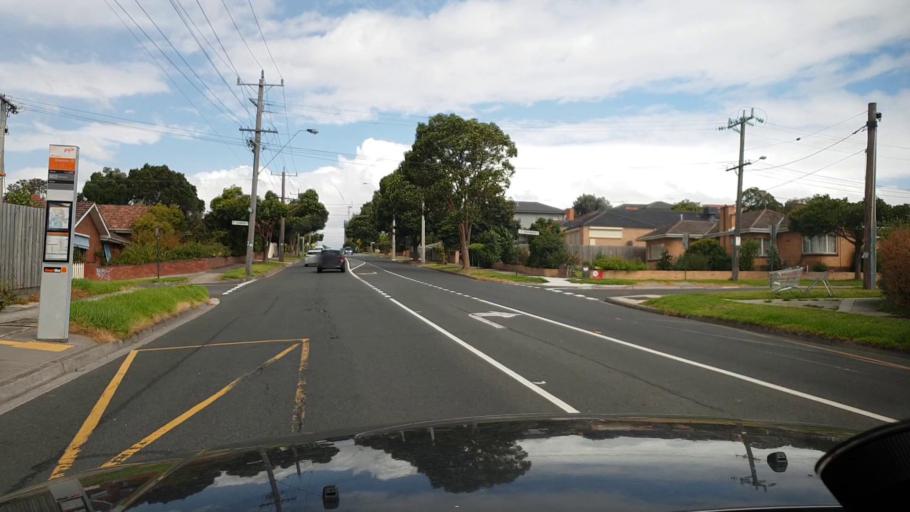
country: AU
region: Victoria
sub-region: Whitehorse
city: Box Hill North
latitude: -37.8081
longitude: 145.1258
